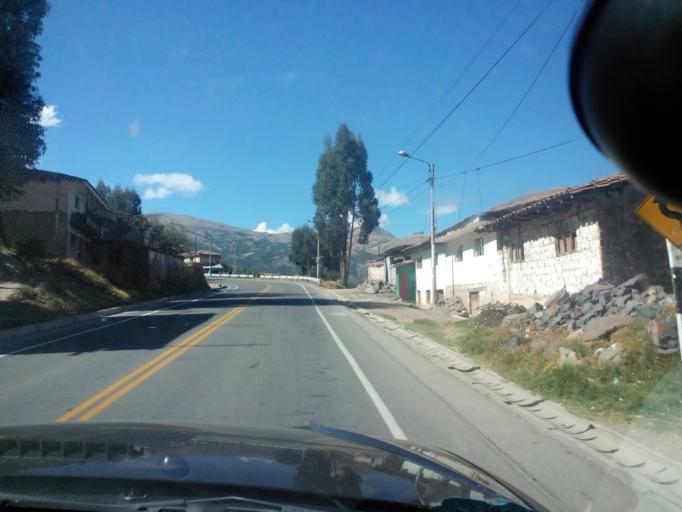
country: PE
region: Cusco
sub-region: Provincia de Quispicanchis
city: Urcos
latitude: -13.6853
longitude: -71.6163
